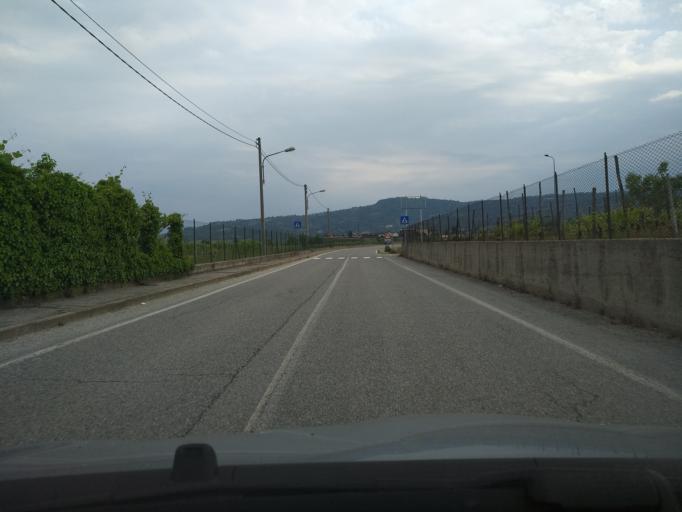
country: IT
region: Piedmont
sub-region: Provincia di Torino
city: Roletto
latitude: 44.9320
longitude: 7.3475
